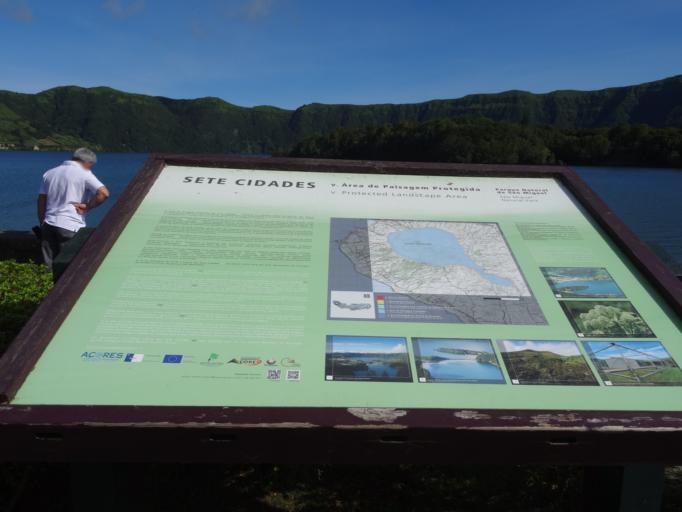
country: PT
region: Azores
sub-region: Ponta Delgada
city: Arrifes
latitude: 37.8554
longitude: -25.7868
